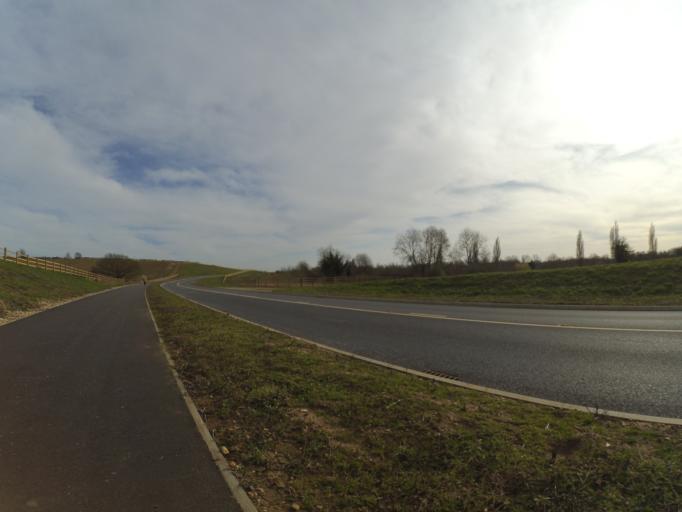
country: GB
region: England
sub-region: Warwickshire
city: Rugby
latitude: 52.3758
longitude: -1.2271
